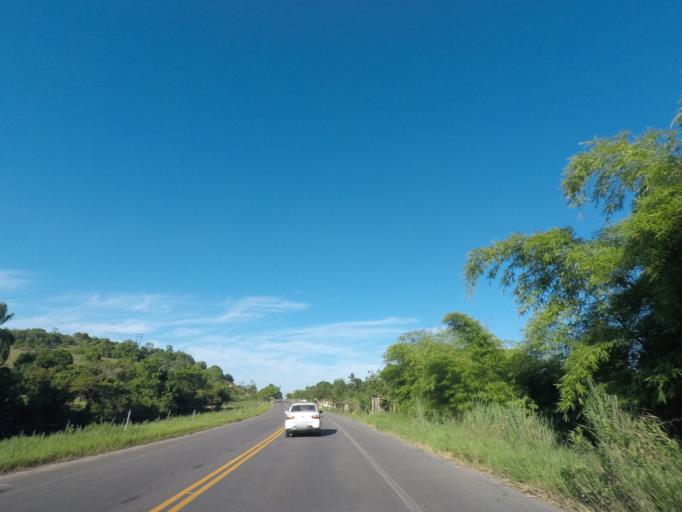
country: BR
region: Bahia
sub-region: Nazare
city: Nazare
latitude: -13.0139
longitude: -38.9755
